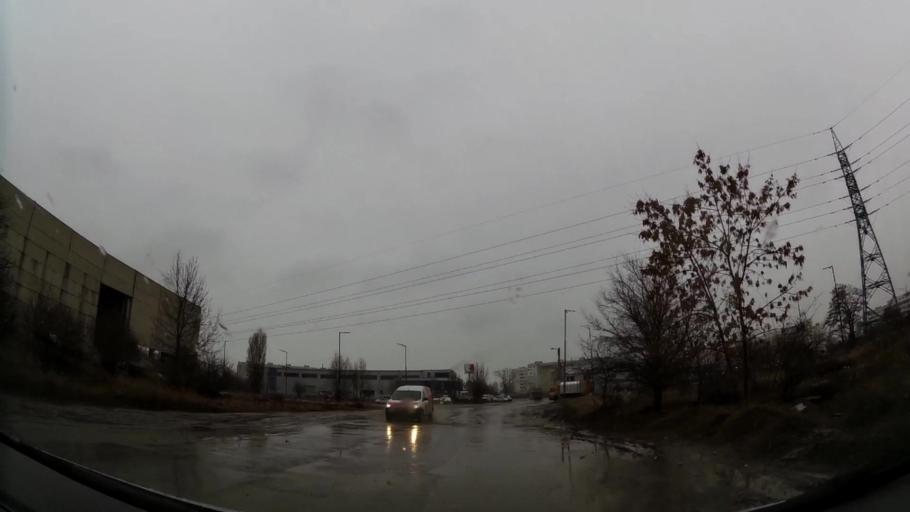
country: BG
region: Sofia-Capital
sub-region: Stolichna Obshtina
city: Sofia
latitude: 42.6474
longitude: 23.4130
